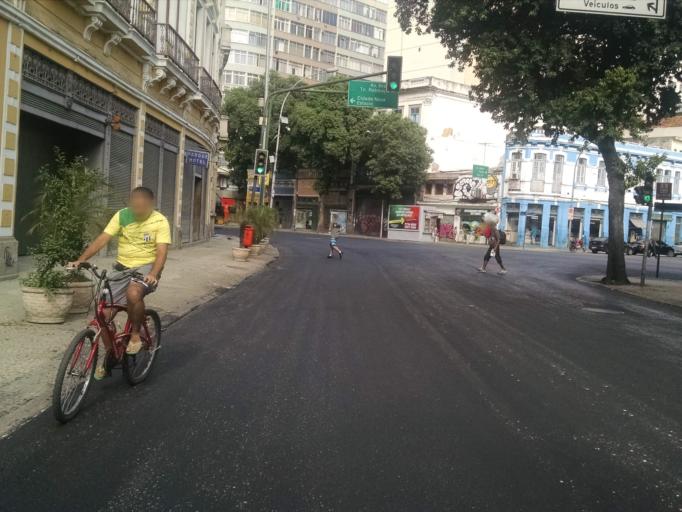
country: BR
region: Rio de Janeiro
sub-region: Rio De Janeiro
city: Rio de Janeiro
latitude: -22.9112
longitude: -43.1926
